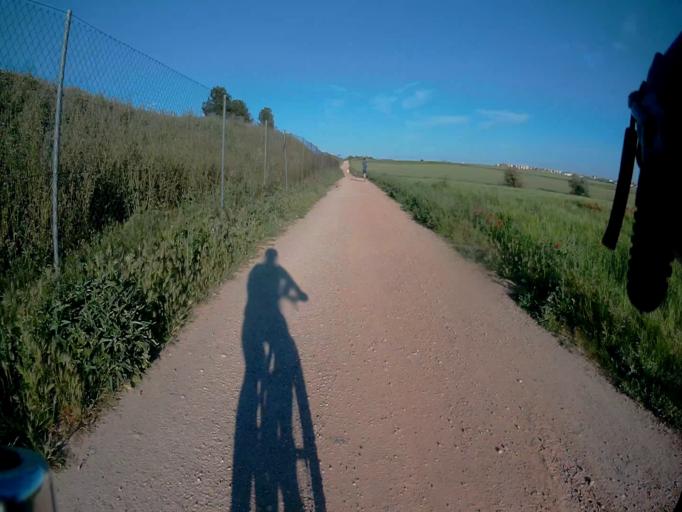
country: ES
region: Madrid
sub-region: Provincia de Madrid
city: Alcorcon
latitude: 40.3218
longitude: -3.8330
